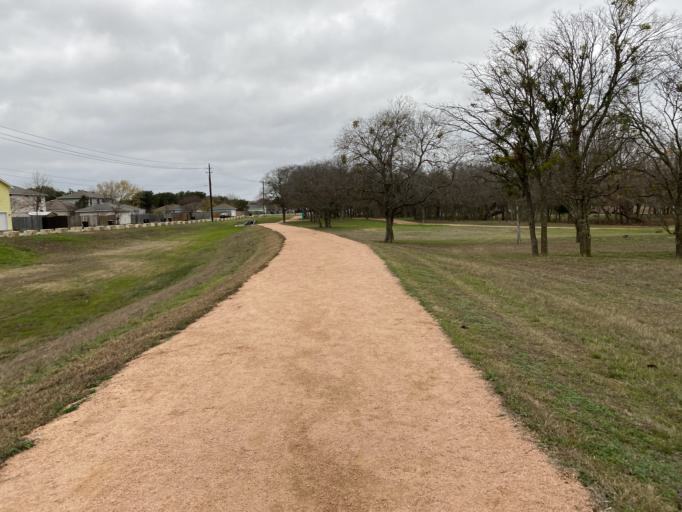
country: US
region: Texas
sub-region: Travis County
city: Wells Branch
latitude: 30.4209
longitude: -97.6551
